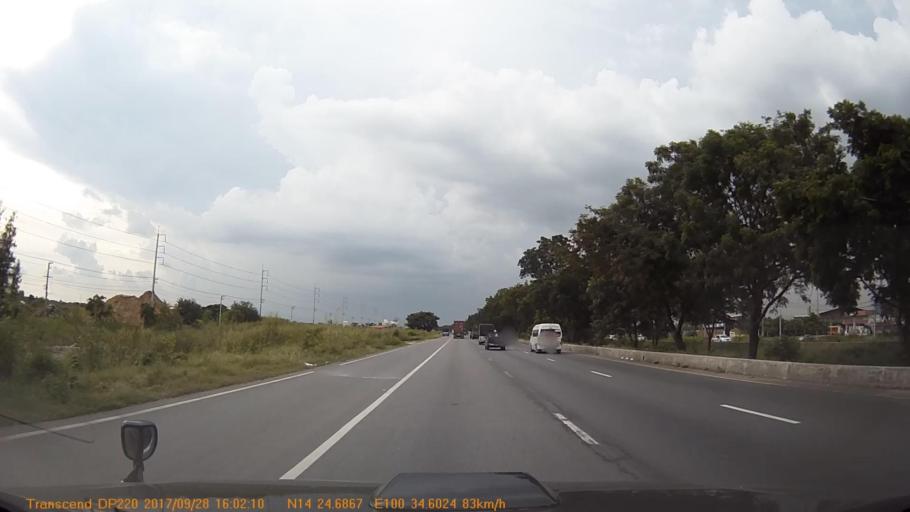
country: TH
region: Phra Nakhon Si Ayutthaya
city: Phra Nakhon Si Ayutthaya
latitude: 14.4113
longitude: 100.5769
